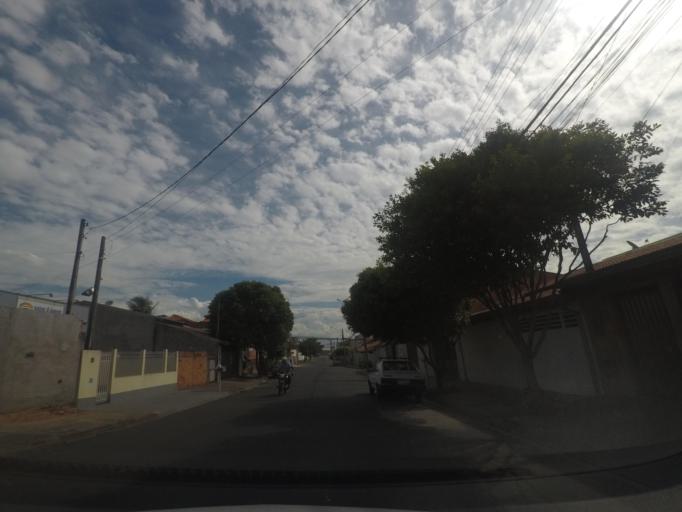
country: BR
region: Sao Paulo
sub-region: Sumare
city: Sumare
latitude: -22.8068
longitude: -47.2699
